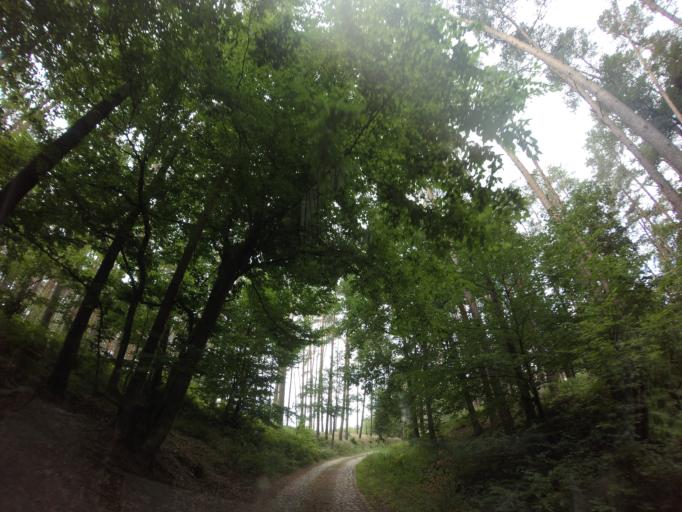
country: PL
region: Lubusz
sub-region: Powiat strzelecko-drezdenecki
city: Strzelce Krajenskie
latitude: 52.9269
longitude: 15.6074
